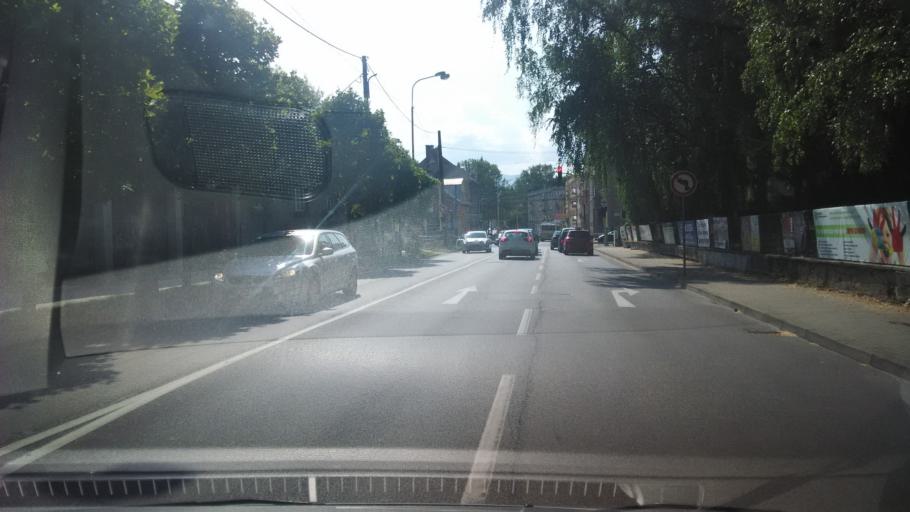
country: SK
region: Zilinsky
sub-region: Okres Zilina
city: Zilina
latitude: 49.2204
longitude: 18.7425
